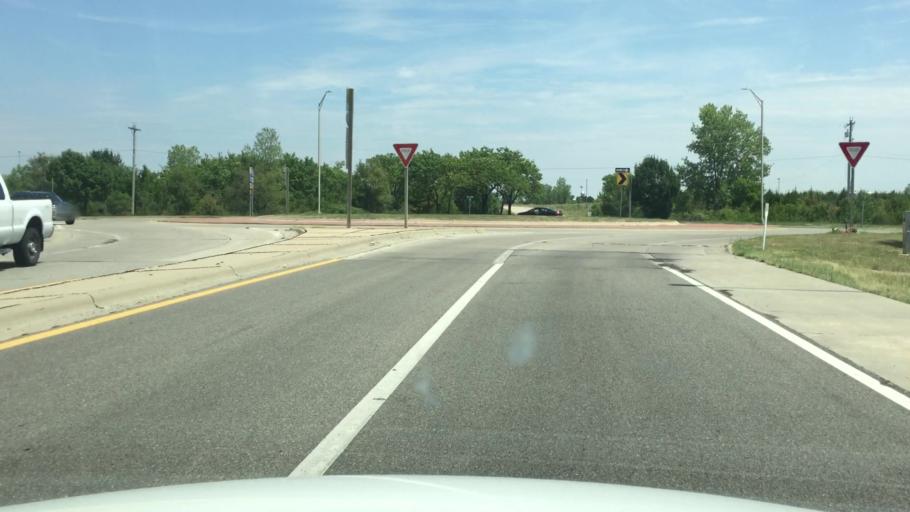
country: US
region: Kansas
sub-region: Shawnee County
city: Topeka
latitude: 39.0318
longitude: -95.6240
